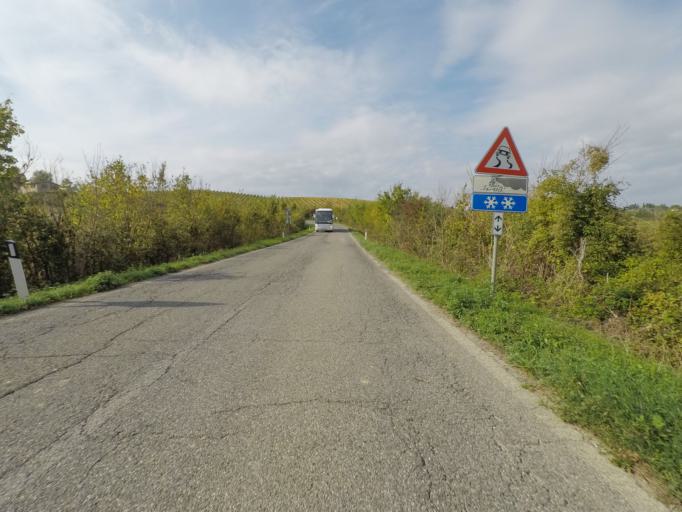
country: IT
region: Tuscany
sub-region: Provincia di Siena
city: Belverde
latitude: 43.3660
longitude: 11.3317
